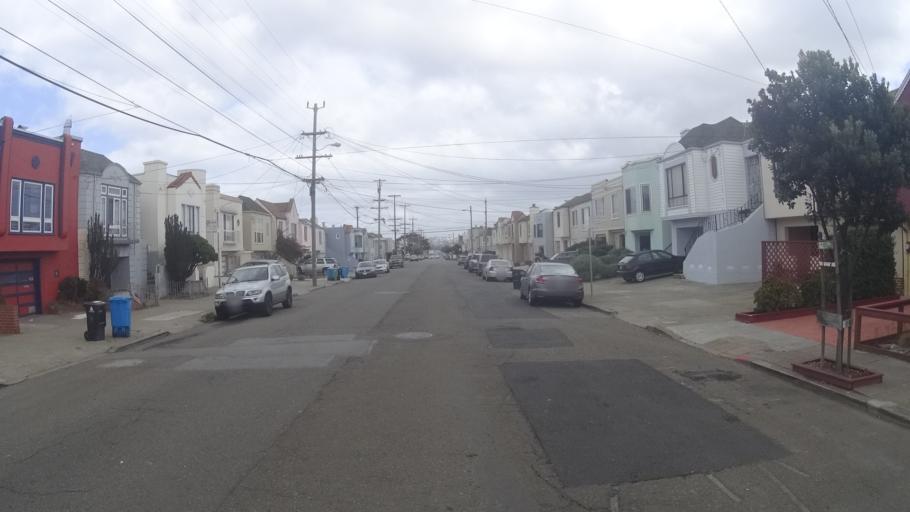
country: US
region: California
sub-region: San Mateo County
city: Daly City
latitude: 37.7426
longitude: -122.5046
